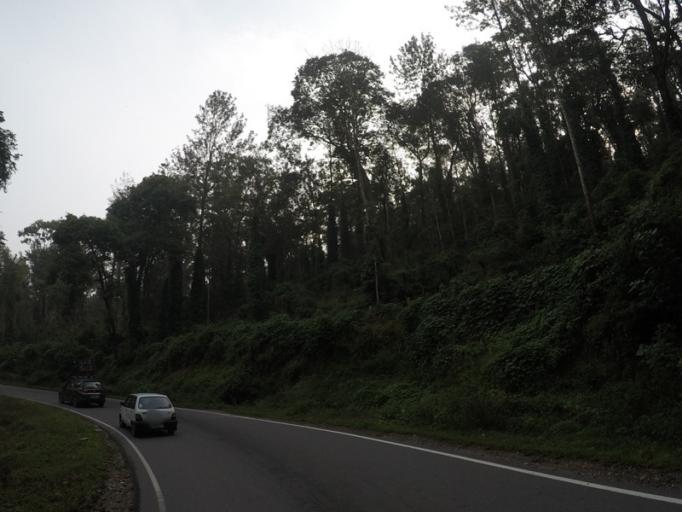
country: IN
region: Karnataka
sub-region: Chikmagalur
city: Mudigere
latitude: 13.2684
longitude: 75.6246
